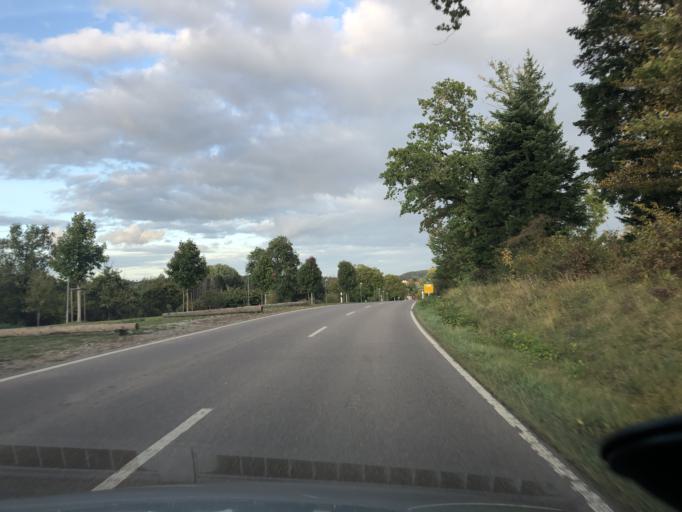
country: DE
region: Baden-Wuerttemberg
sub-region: Karlsruhe Region
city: Wimsheim
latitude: 48.8456
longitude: 8.8202
